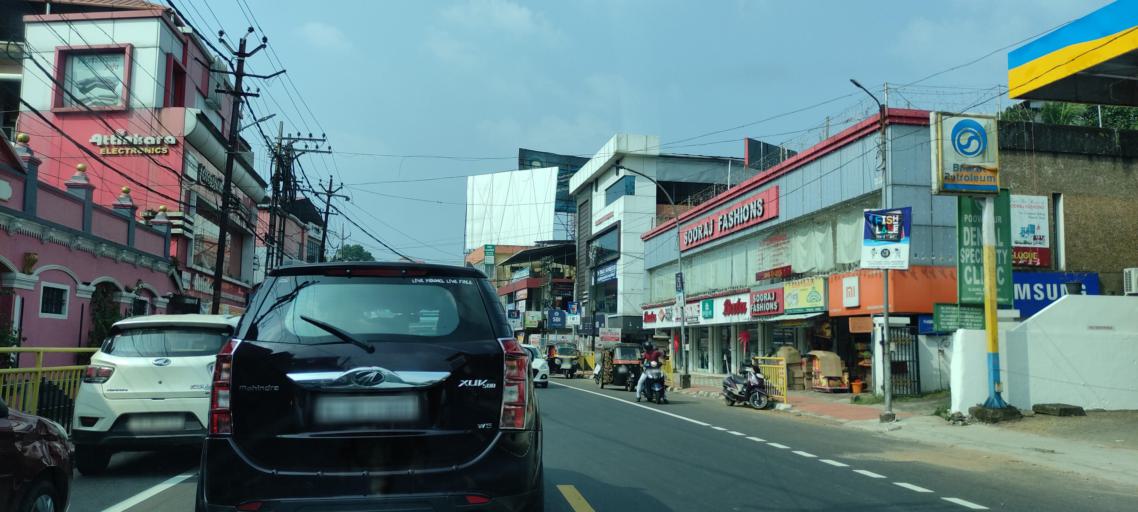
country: IN
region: Kerala
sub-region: Alappuzha
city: Chengannur
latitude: 9.3168
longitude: 76.6164
